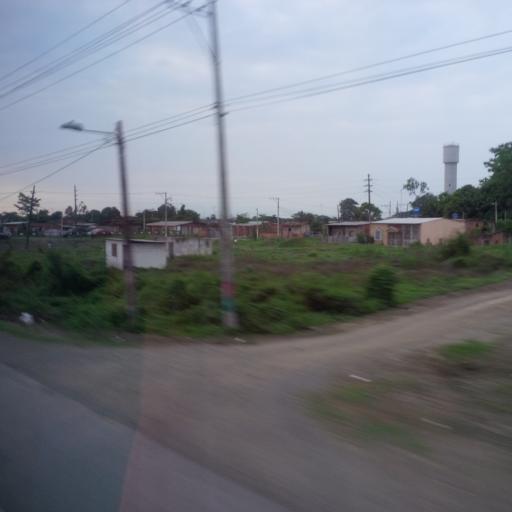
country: EC
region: Canar
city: La Troncal
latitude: -2.3273
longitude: -79.4104
